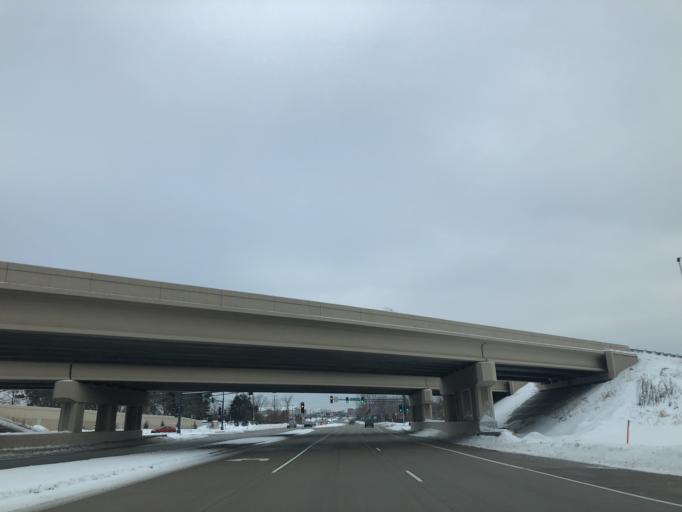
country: US
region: Minnesota
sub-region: Ramsey County
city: Shoreview
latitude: 45.0793
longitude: -93.1757
